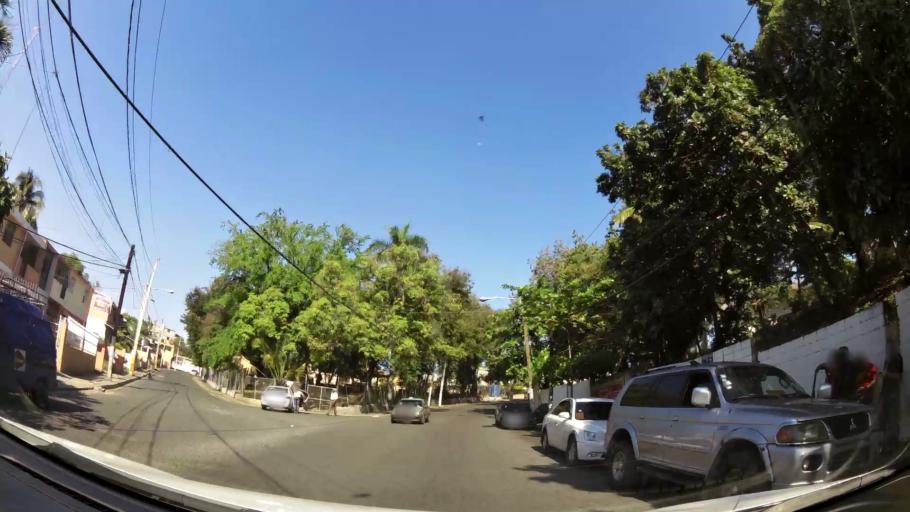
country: DO
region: Nacional
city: Santo Domingo
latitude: 18.4735
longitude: -69.9932
